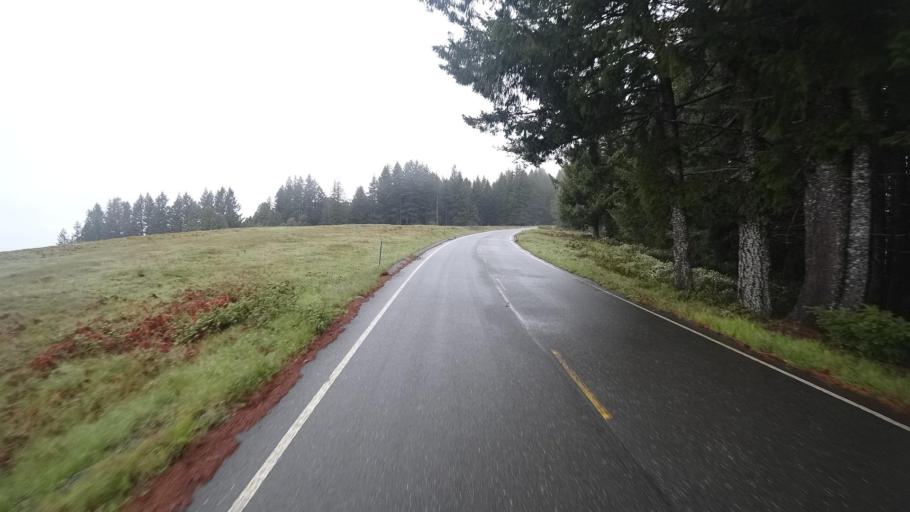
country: US
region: California
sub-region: Humboldt County
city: Westhaven-Moonstone
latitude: 41.1946
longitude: -123.9412
